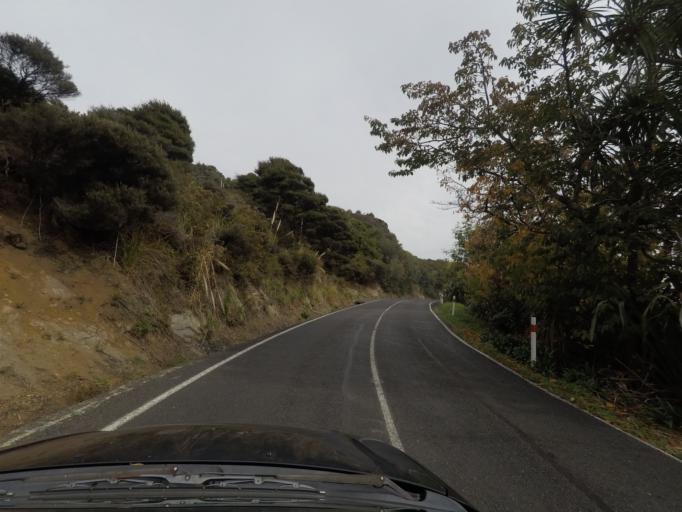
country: NZ
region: Auckland
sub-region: Auckland
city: Muriwai Beach
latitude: -36.9619
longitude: 174.4751
